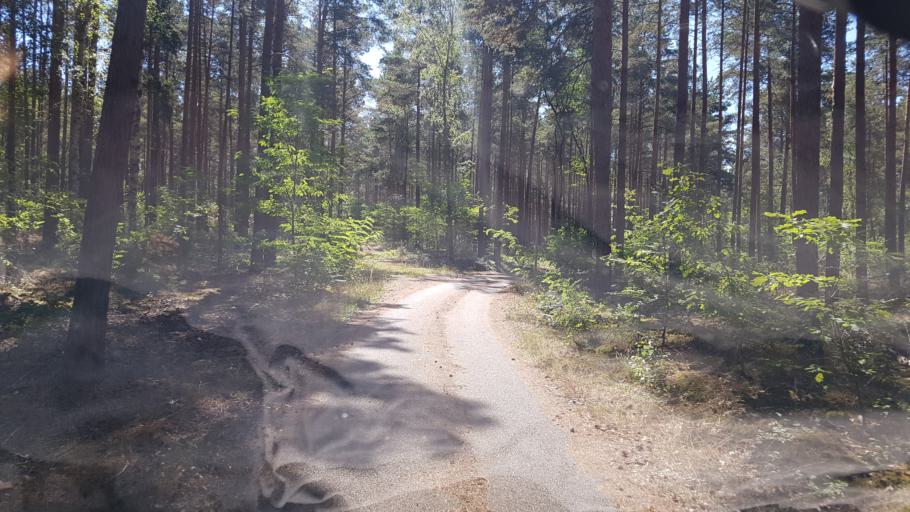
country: DE
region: Brandenburg
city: Calau
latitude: 51.7058
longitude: 13.9993
